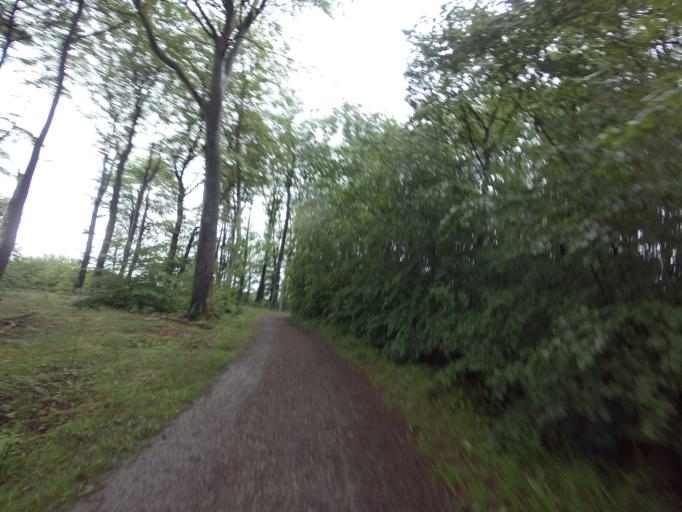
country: SE
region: Skane
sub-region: Helsingborg
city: Odakra
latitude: 56.0912
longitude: 12.7312
